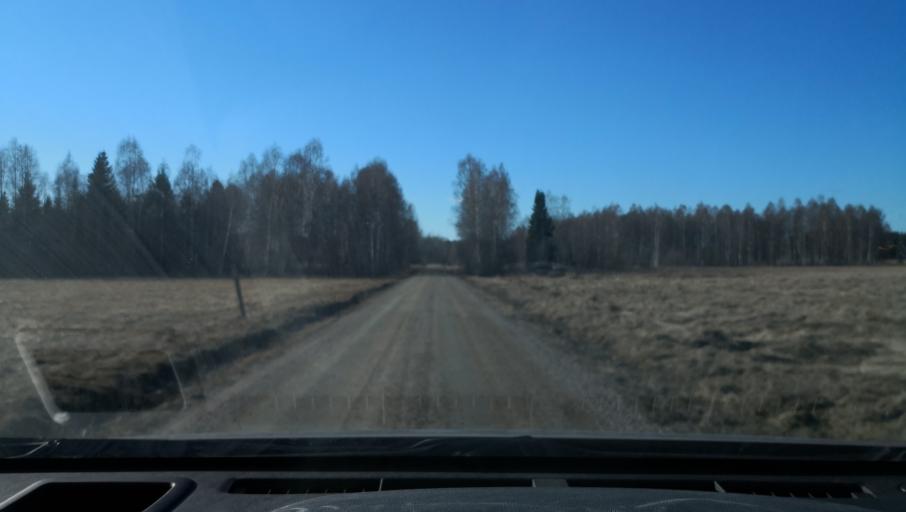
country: SE
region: Vaestmanland
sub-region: Sala Kommun
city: Sala
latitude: 60.1209
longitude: 16.6633
